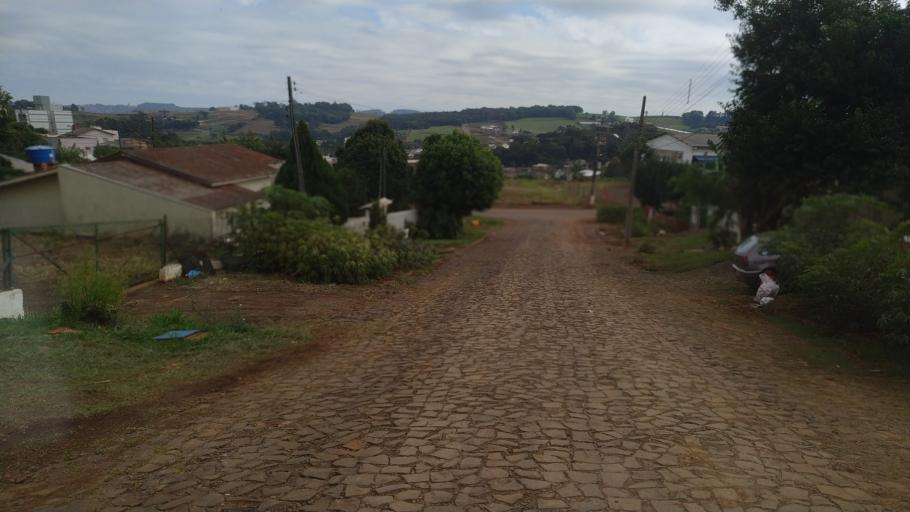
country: BR
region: Santa Catarina
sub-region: Chapeco
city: Chapeco
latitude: -27.0685
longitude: -52.6064
